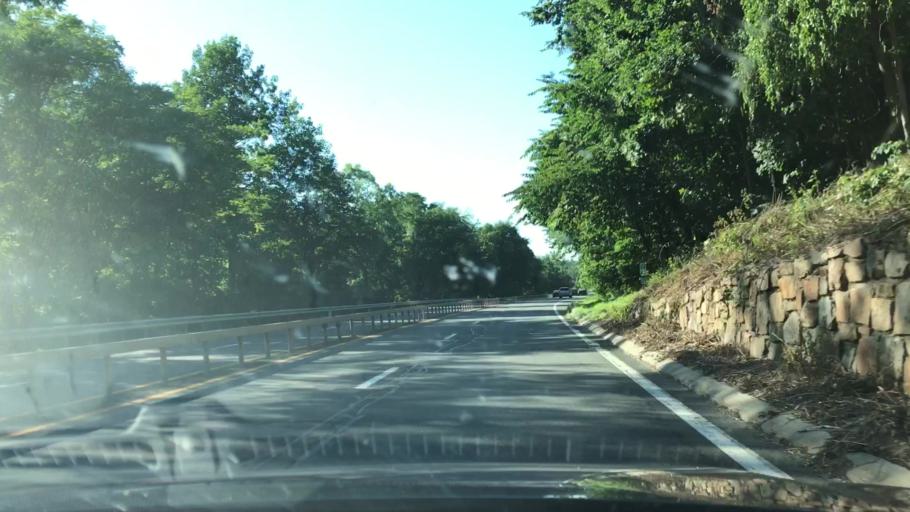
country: US
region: New York
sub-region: Westchester County
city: Valhalla
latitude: 41.0786
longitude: -73.7798
